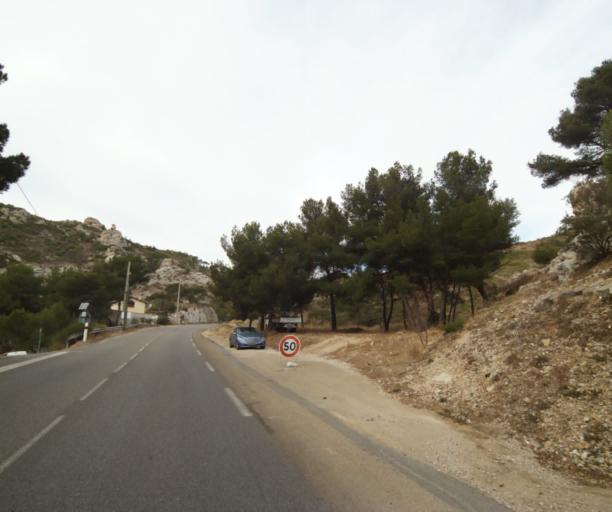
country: FR
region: Provence-Alpes-Cote d'Azur
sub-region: Departement des Bouches-du-Rhone
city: Le Rove
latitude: 43.3593
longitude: 5.2742
